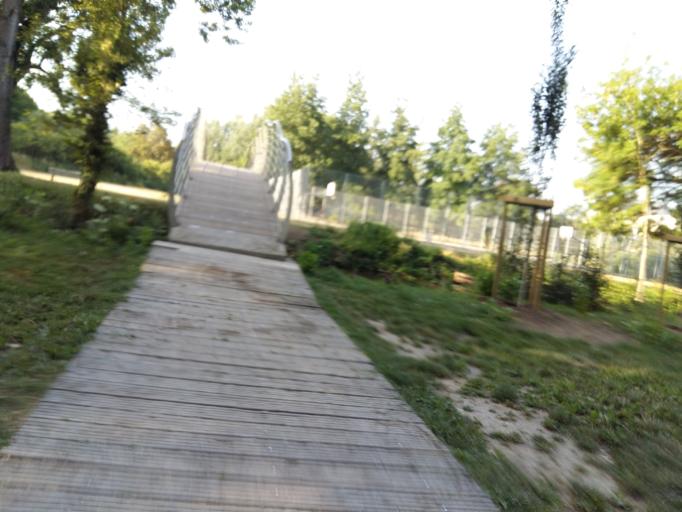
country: FR
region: Picardie
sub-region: Departement de la Somme
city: Amiens
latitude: 49.8977
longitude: 2.3092
